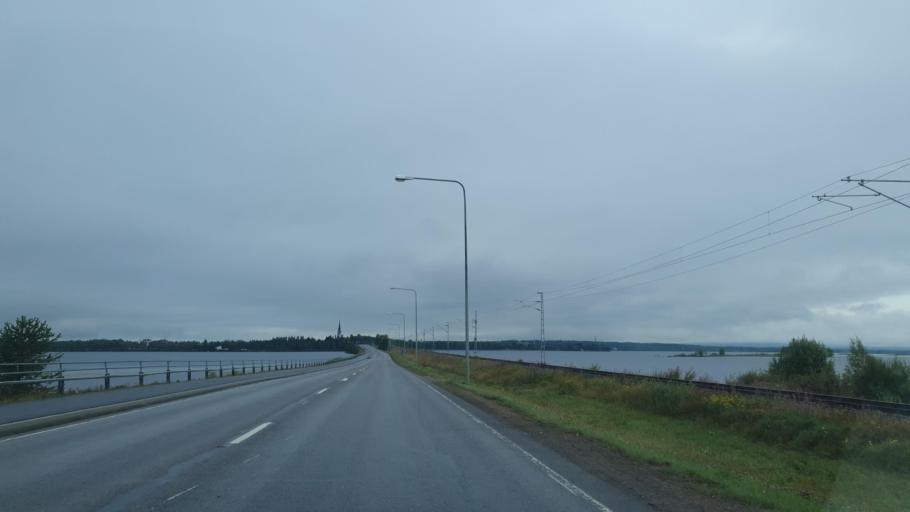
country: FI
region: Lapland
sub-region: Itae-Lappi
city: Kemijaervi
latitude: 66.7157
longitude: 27.4690
